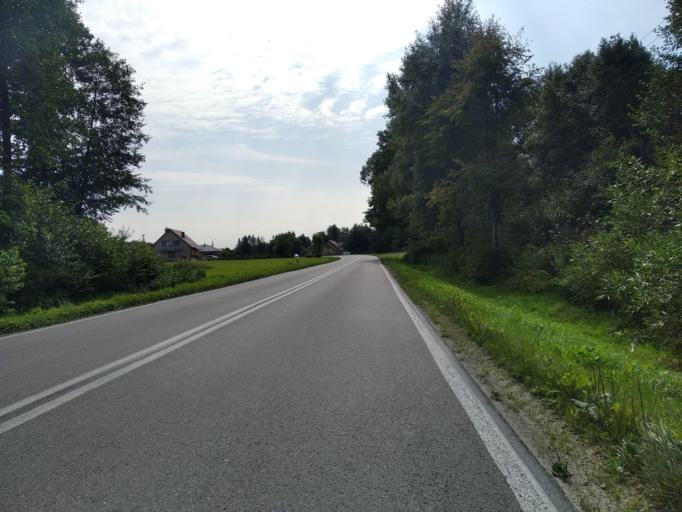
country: PL
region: Subcarpathian Voivodeship
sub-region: Powiat ropczycko-sedziszowski
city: Ostrow
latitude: 50.1168
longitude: 21.5852
